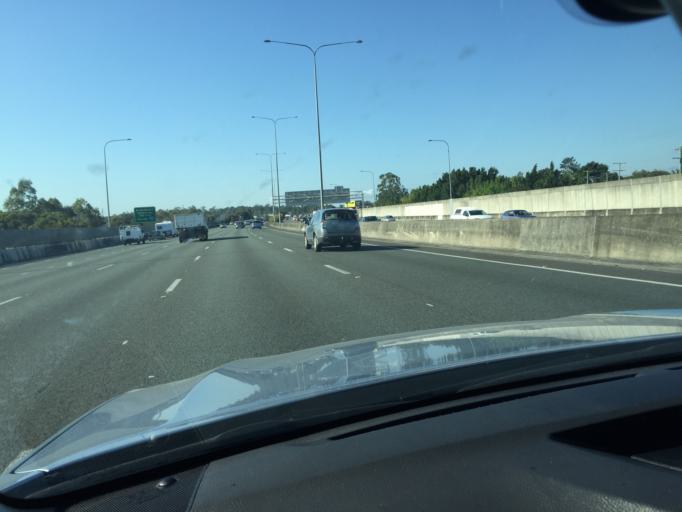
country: AU
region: Queensland
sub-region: Logan
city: Beenleigh
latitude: -27.6917
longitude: 153.1929
